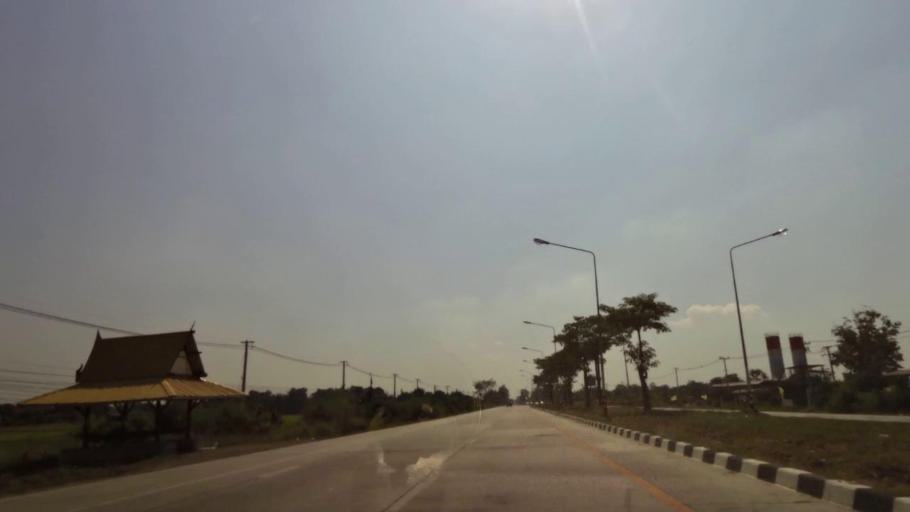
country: TH
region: Phichit
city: Bueng Na Rang
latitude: 16.2673
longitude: 100.1264
